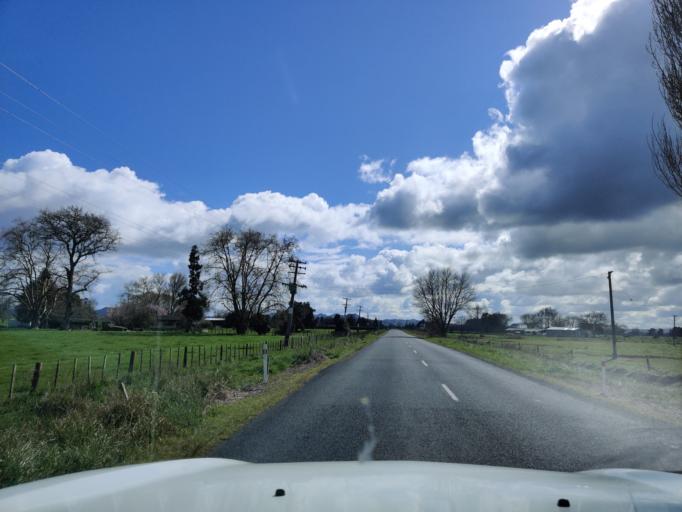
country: NZ
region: Waikato
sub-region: Waikato District
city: Ngaruawahia
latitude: -37.5987
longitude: 175.2983
